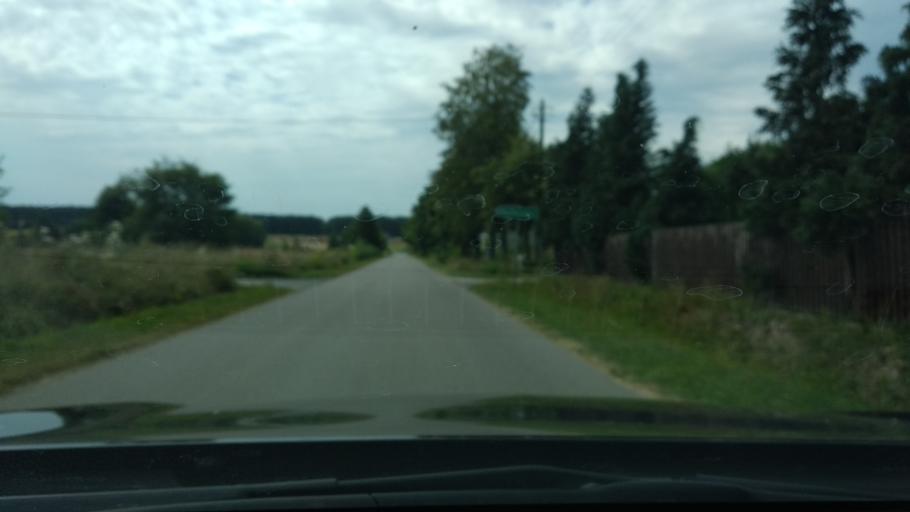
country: PL
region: Masovian Voivodeship
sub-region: Powiat pultuski
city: Zatory
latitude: 52.6485
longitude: 21.1851
